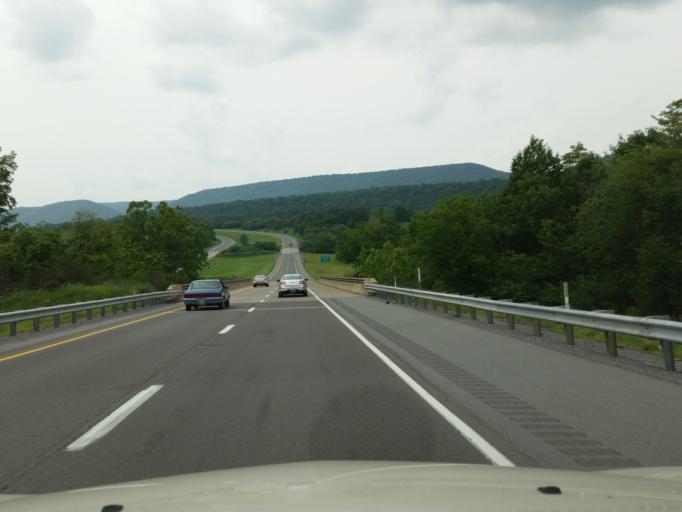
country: US
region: Pennsylvania
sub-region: Juniata County
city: Mifflintown
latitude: 40.6005
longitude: -77.3884
